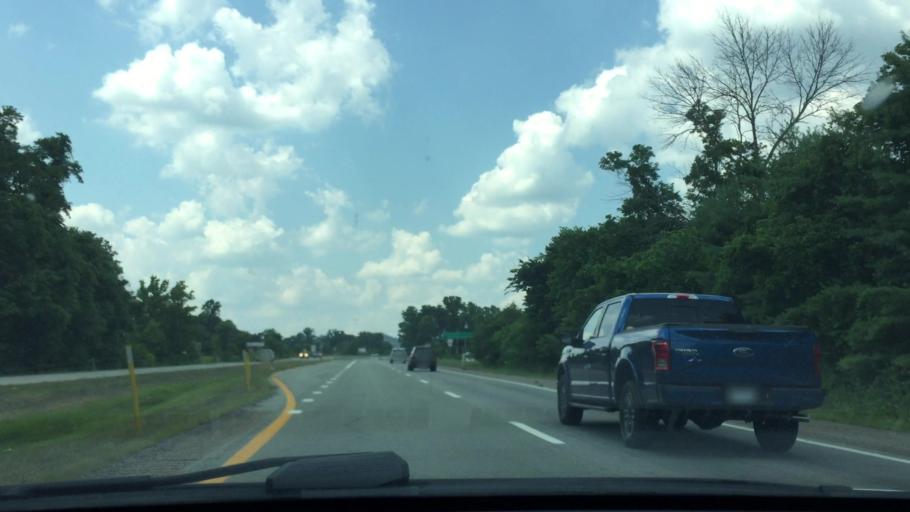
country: US
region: Ohio
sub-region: Belmont County
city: Powhatan Point
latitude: 39.8916
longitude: -80.7901
